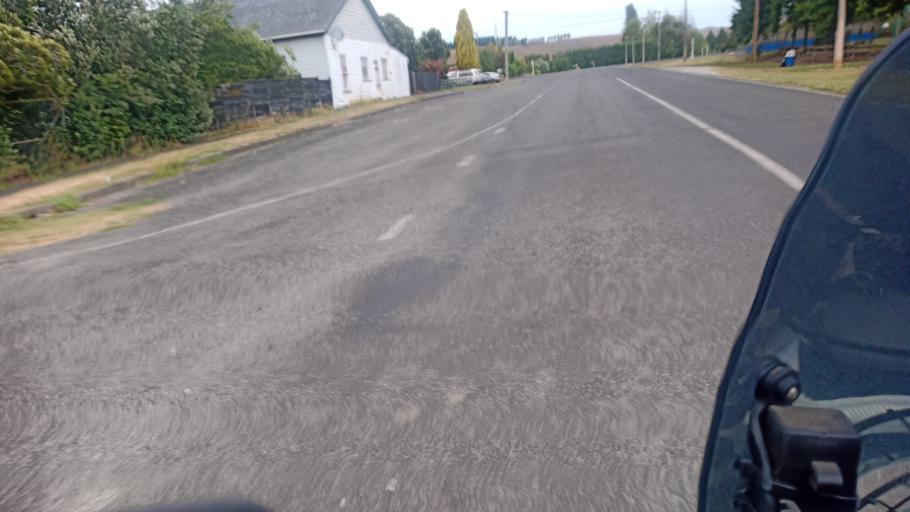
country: NZ
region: Gisborne
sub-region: Gisborne District
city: Gisborne
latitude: -38.6237
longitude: 177.8901
